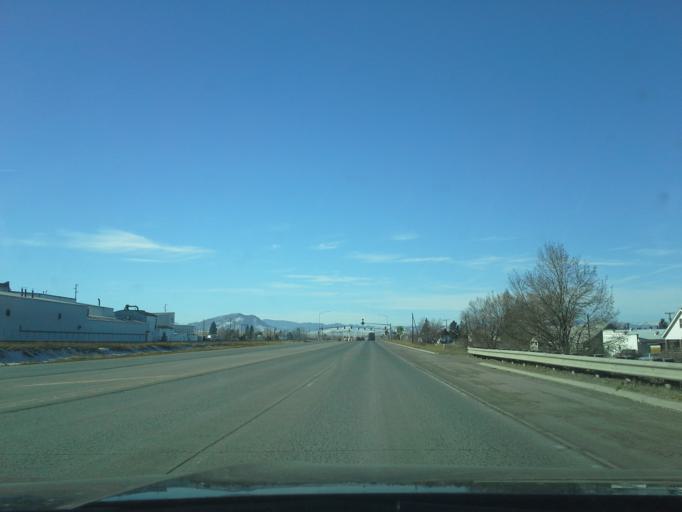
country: US
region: Montana
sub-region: Lewis and Clark County
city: East Helena
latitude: 46.5880
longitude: -111.9201
